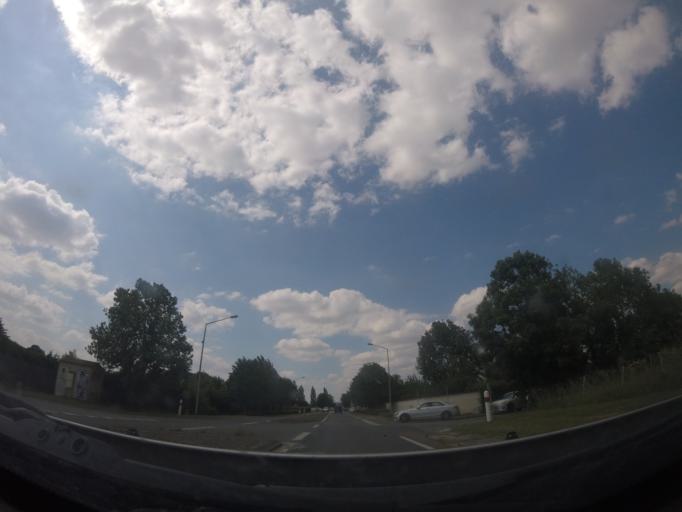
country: FR
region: Poitou-Charentes
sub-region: Departement de la Charente-Maritime
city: Bords
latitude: 45.8555
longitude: -0.8293
